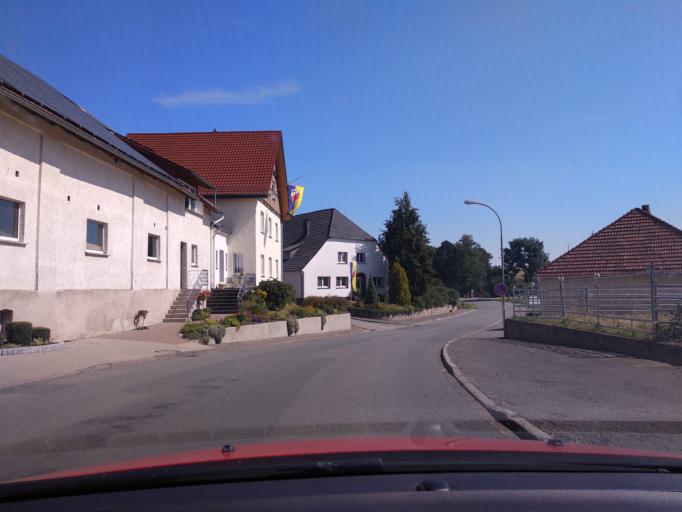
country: DE
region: North Rhine-Westphalia
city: Brakel
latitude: 51.6481
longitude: 9.2143
